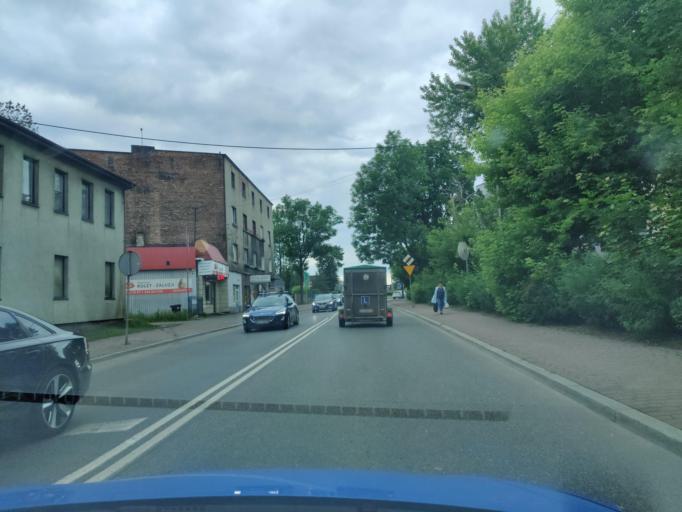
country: PL
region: Silesian Voivodeship
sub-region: Myslowice
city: Myslowice
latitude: 50.2370
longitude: 19.1589
